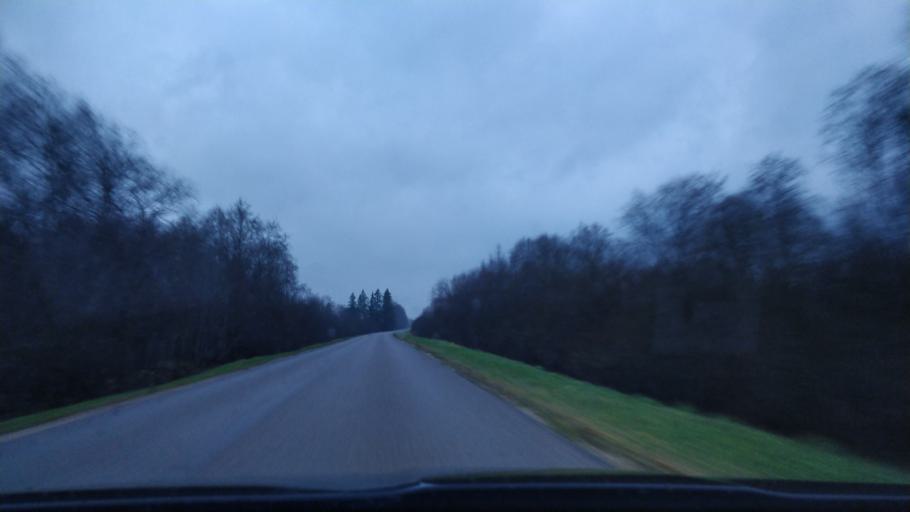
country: EE
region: Laeaene
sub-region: Lihula vald
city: Lihula
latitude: 58.7029
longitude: 23.8602
